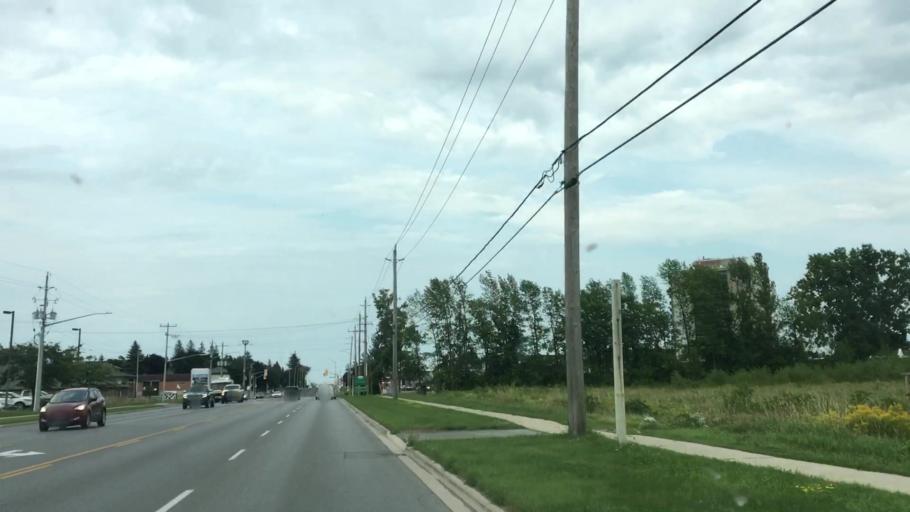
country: CA
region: Ontario
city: Quinte West
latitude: 44.0939
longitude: -77.6003
